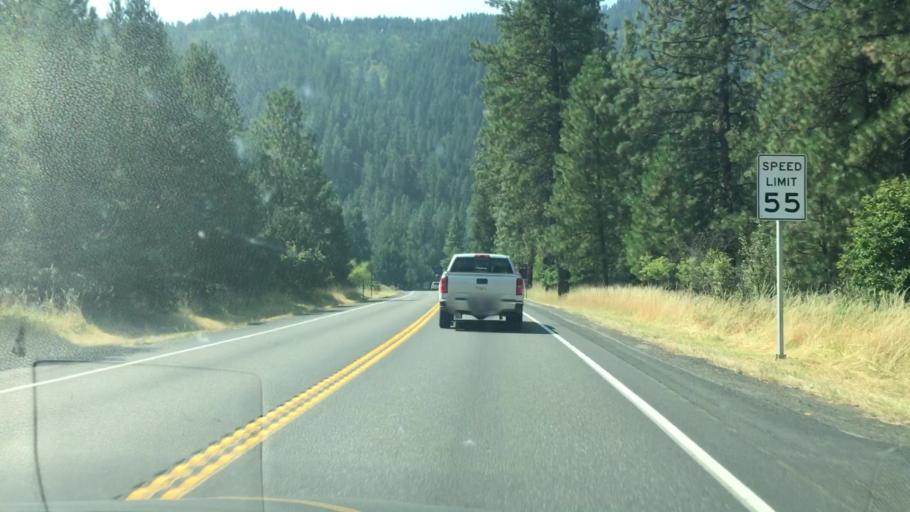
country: US
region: Idaho
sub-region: Clearwater County
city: Orofino
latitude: 46.4945
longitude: -116.4489
